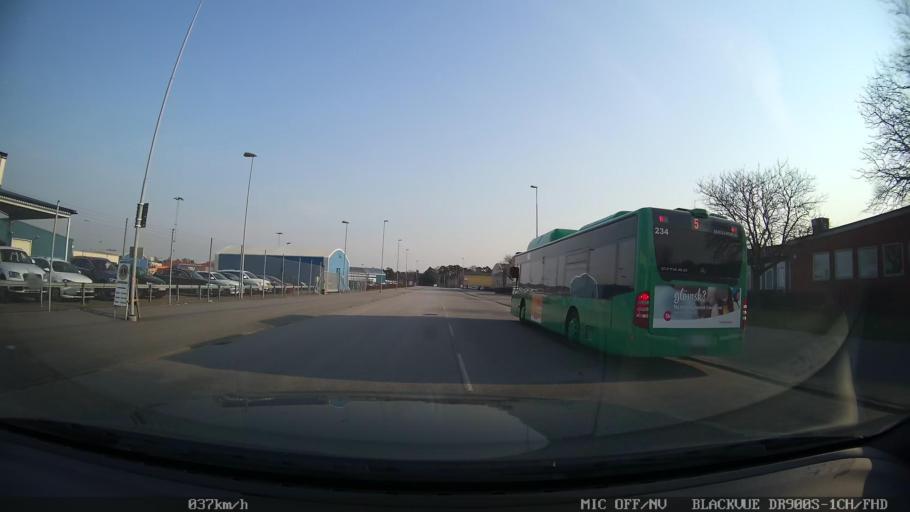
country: SE
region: Skane
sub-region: Ystads Kommun
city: Ystad
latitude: 55.4251
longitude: 13.8394
